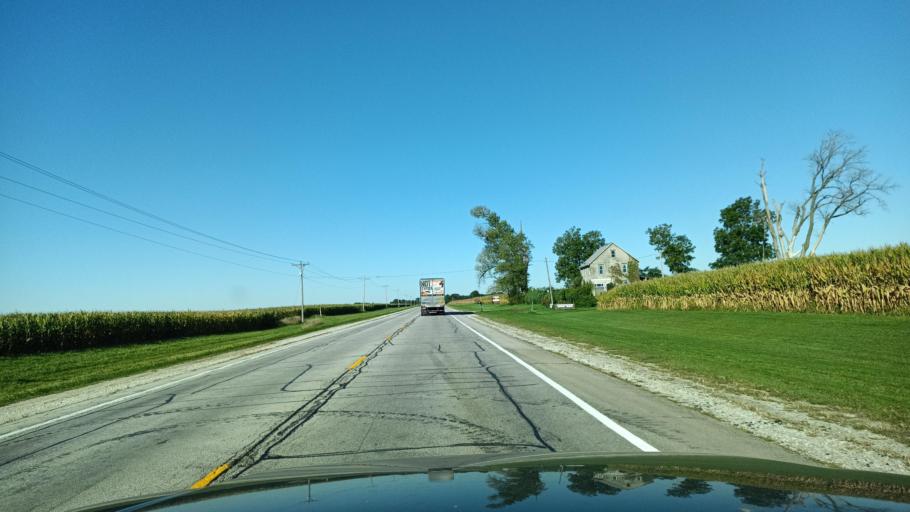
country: US
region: Illinois
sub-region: Warren County
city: Monmouth
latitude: 40.8783
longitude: -90.6929
